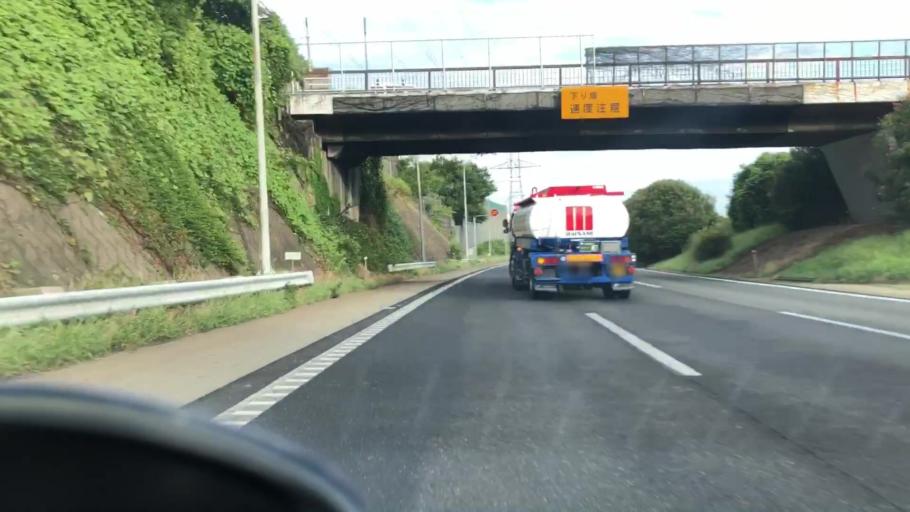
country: JP
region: Hyogo
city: Takarazuka
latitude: 34.8162
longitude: 135.3560
